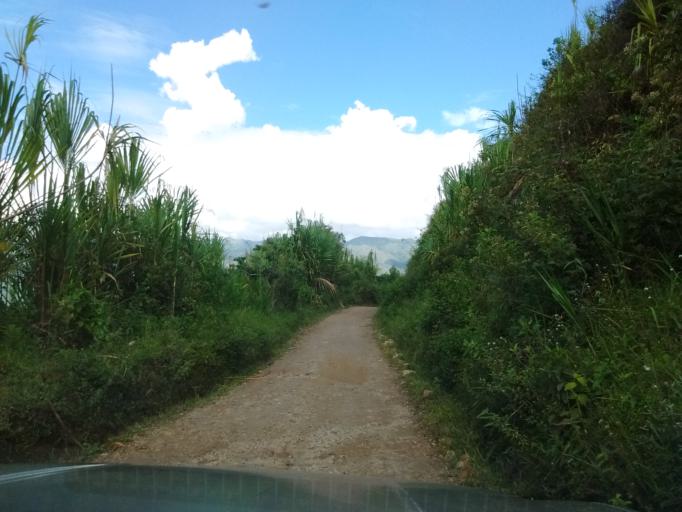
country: CO
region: Cauca
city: Morales
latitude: 2.6879
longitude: -76.7386
